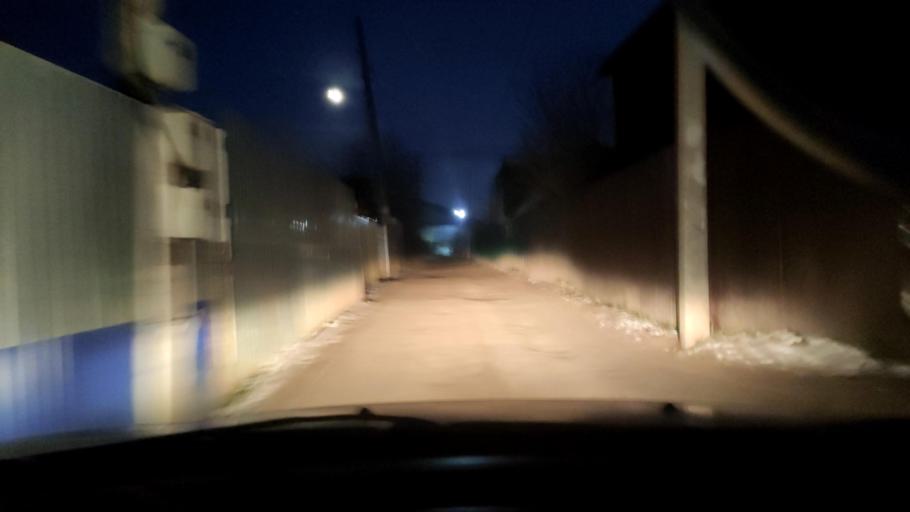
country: RU
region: Perm
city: Kondratovo
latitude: 57.9548
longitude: 56.0965
